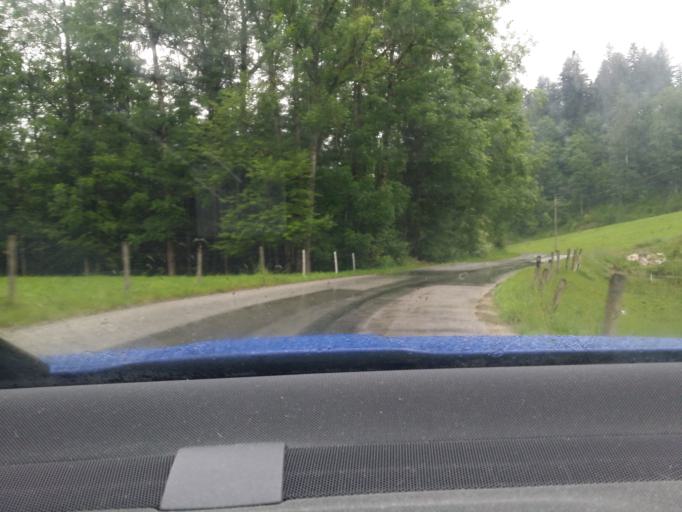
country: AT
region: Salzburg
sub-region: Politischer Bezirk Hallein
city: Abtenau
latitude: 47.5891
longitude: 13.3419
